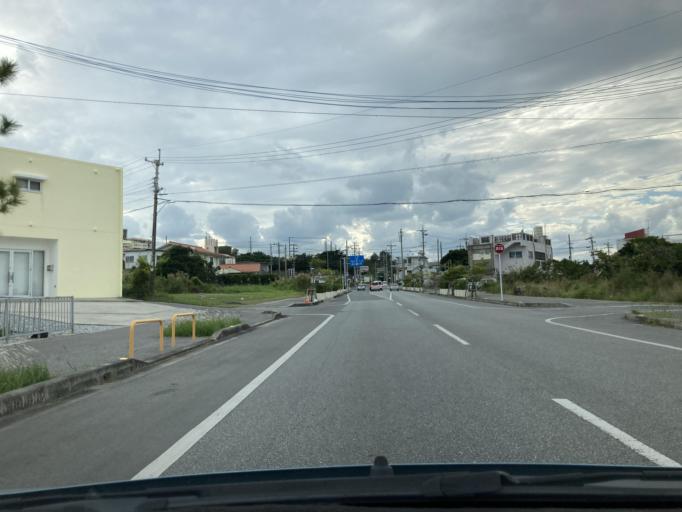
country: JP
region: Okinawa
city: Katsuren-haebaru
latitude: 26.3305
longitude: 127.8855
